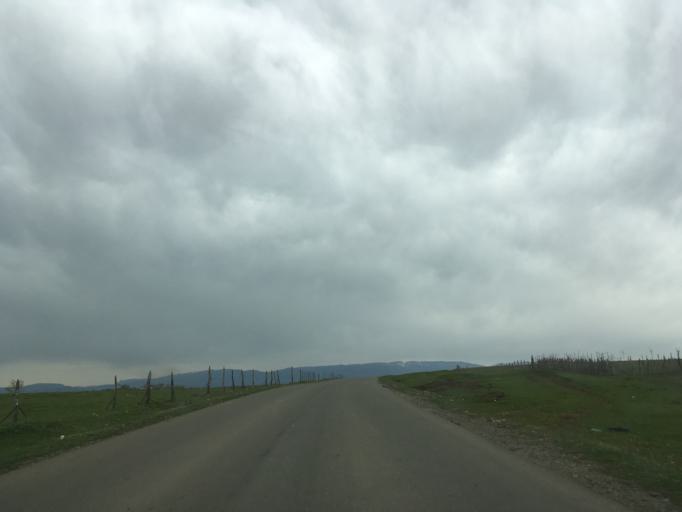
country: GE
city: Surami
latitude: 42.2059
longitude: 43.3937
